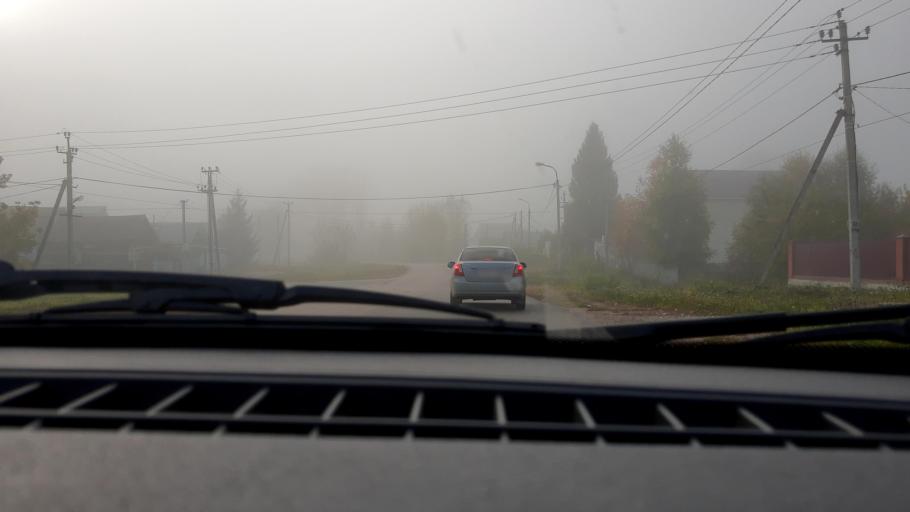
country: RU
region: Bashkortostan
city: Mikhaylovka
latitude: 54.7618
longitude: 55.9001
